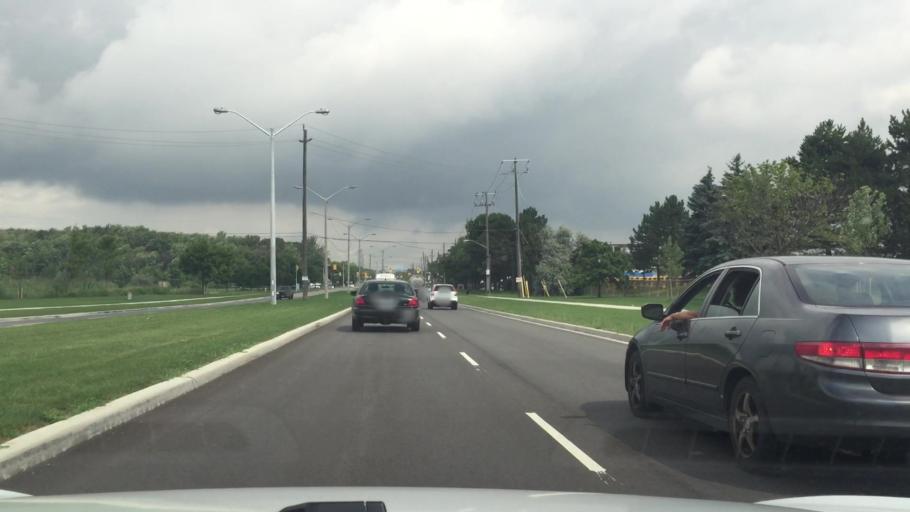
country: CA
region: Ontario
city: Concord
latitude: 43.7691
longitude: -79.4955
